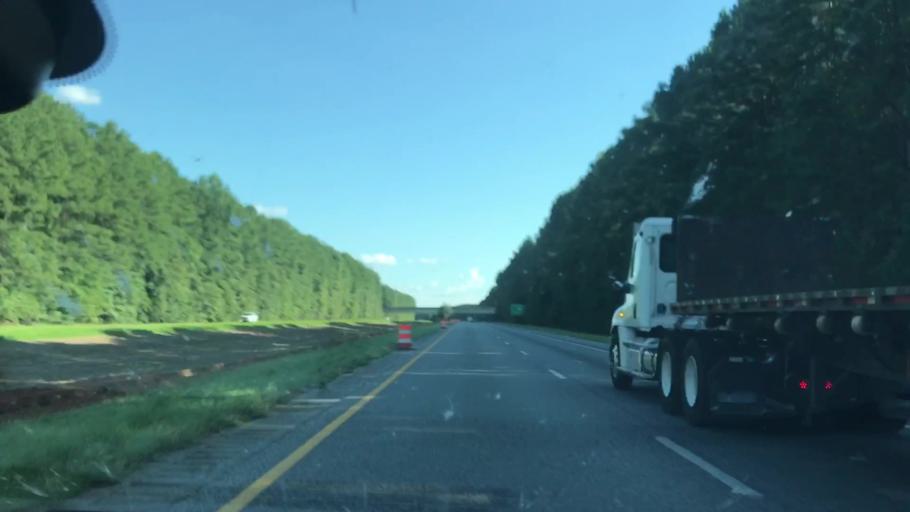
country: US
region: Georgia
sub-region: Harris County
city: Hamilton
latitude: 32.6834
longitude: -84.9903
